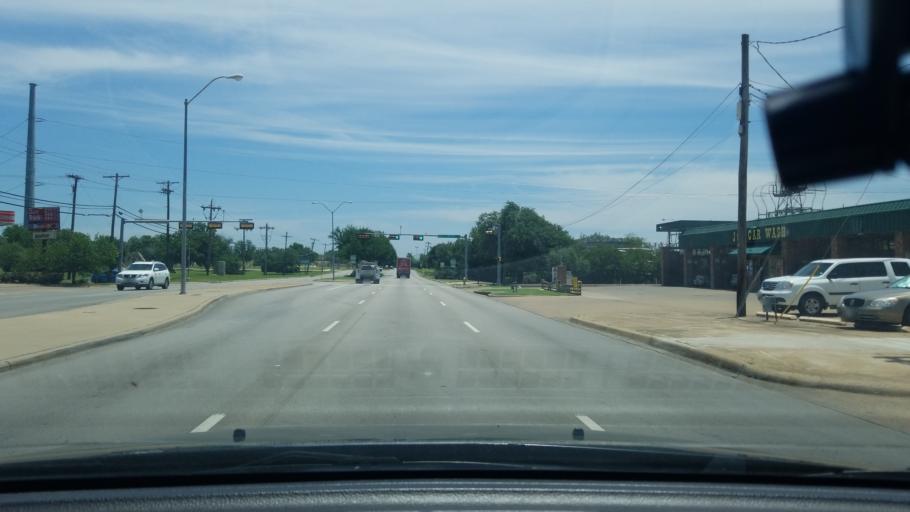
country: US
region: Texas
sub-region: Dallas County
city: Mesquite
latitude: 32.7765
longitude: -96.6189
